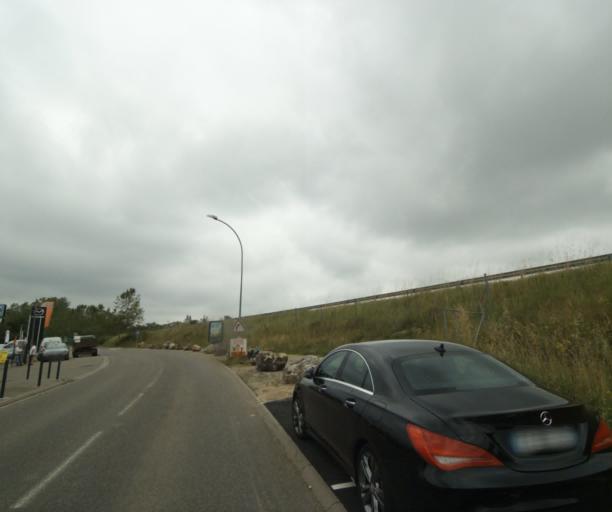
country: FR
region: Midi-Pyrenees
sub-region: Departement du Tarn-et-Garonne
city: Bressols
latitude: 43.9906
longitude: 1.3368
